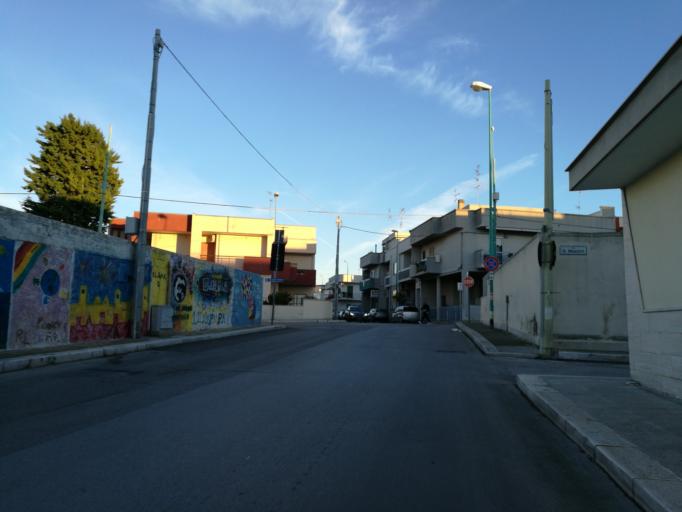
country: IT
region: Apulia
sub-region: Provincia di Bari
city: Adelfia
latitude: 41.0068
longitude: 16.8774
